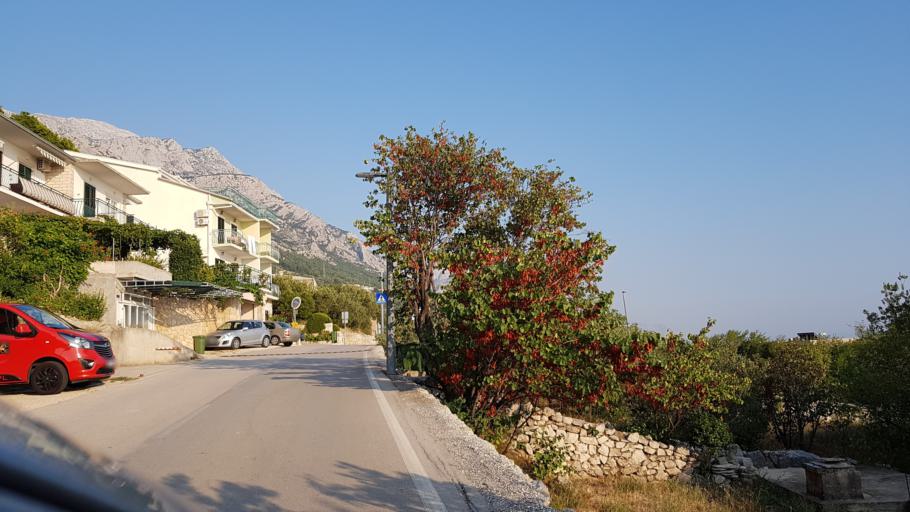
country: HR
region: Splitsko-Dalmatinska
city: Donja Brela
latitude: 43.3834
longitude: 16.9106
